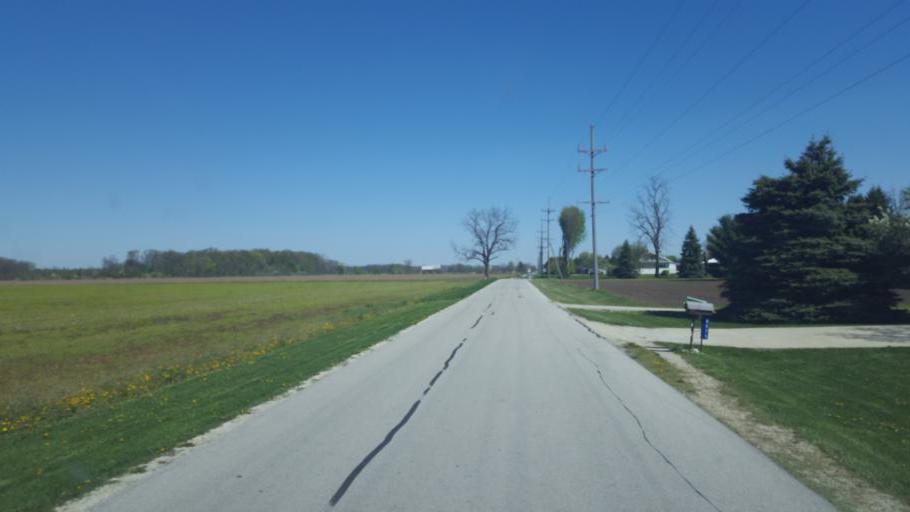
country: US
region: Ohio
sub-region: Sandusky County
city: Ballville
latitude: 41.2535
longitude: -83.1877
